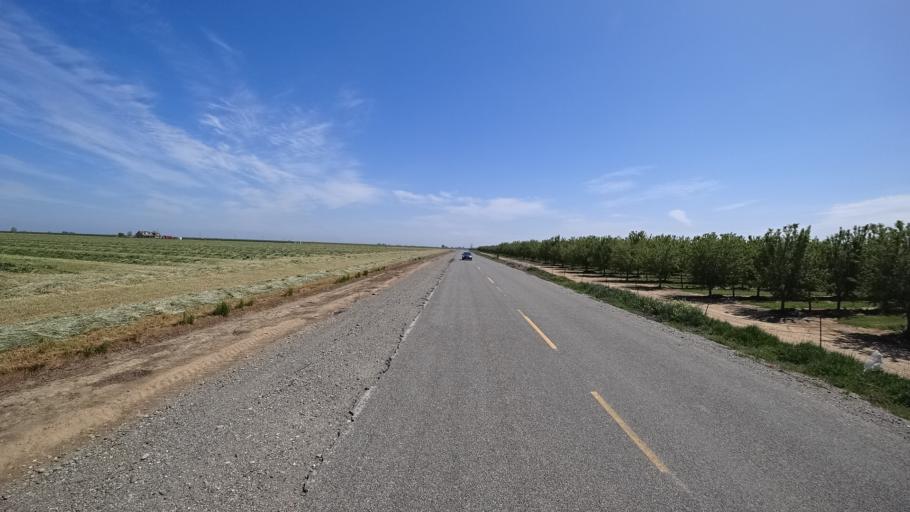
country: US
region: California
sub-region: Glenn County
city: Orland
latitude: 39.6528
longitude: -122.1500
